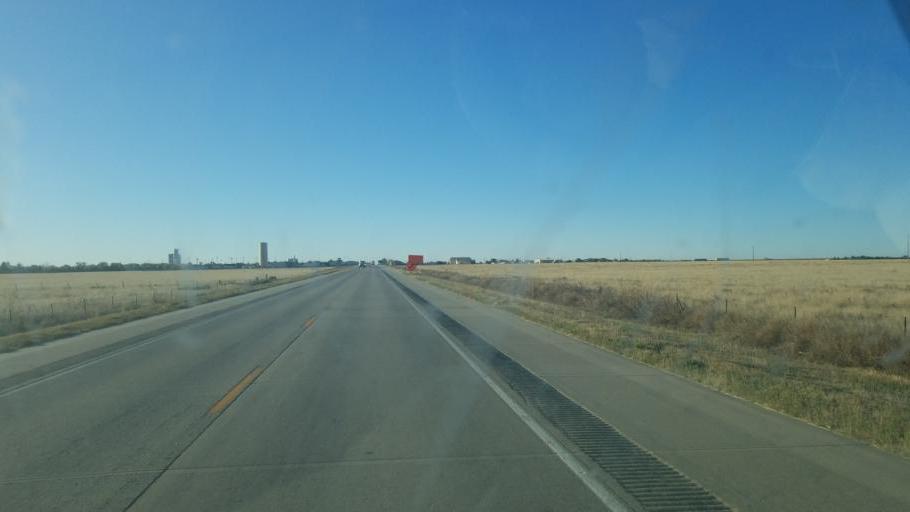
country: US
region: Colorado
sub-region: Kiowa County
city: Eads
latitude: 38.4957
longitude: -102.7857
